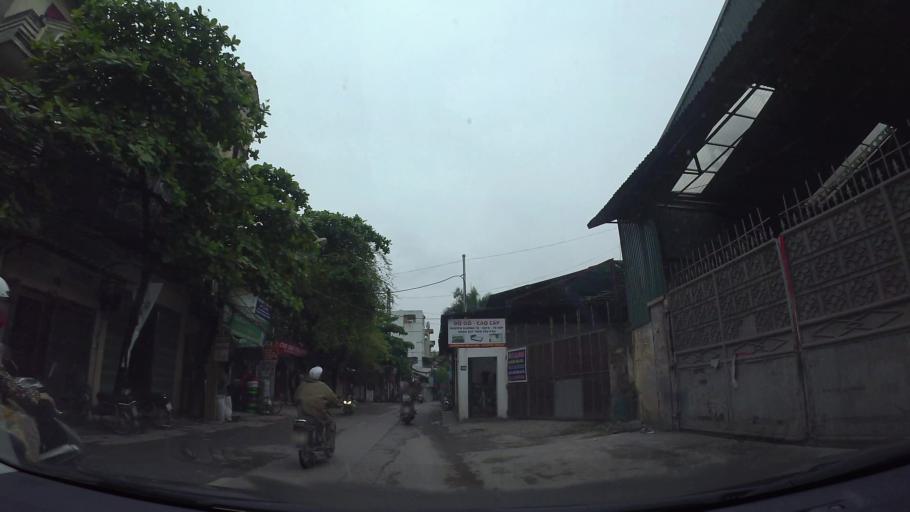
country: VN
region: Ha Noi
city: Hai BaTrung
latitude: 20.9947
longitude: 105.8800
